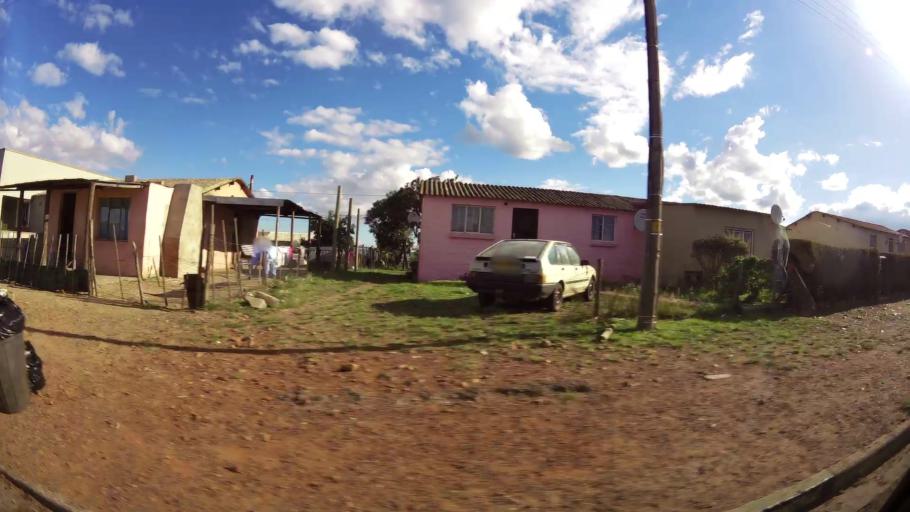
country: ZA
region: Western Cape
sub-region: Overberg District Municipality
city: Swellendam
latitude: -34.0403
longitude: 20.4408
